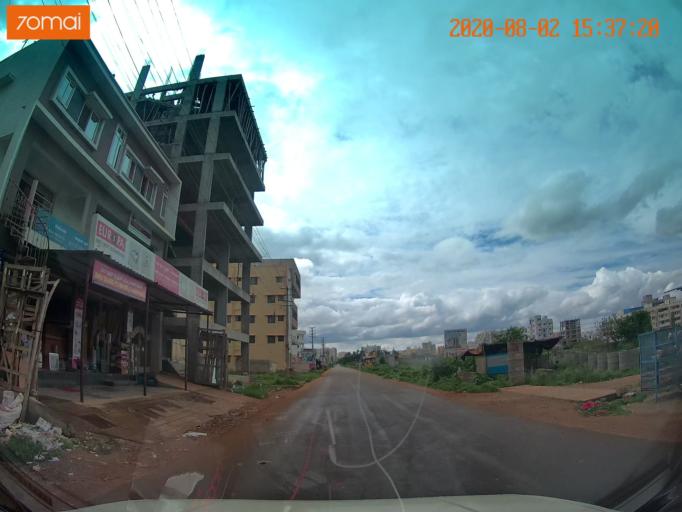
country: IN
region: Karnataka
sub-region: Bangalore Urban
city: Anekal
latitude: 12.8330
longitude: 77.6474
